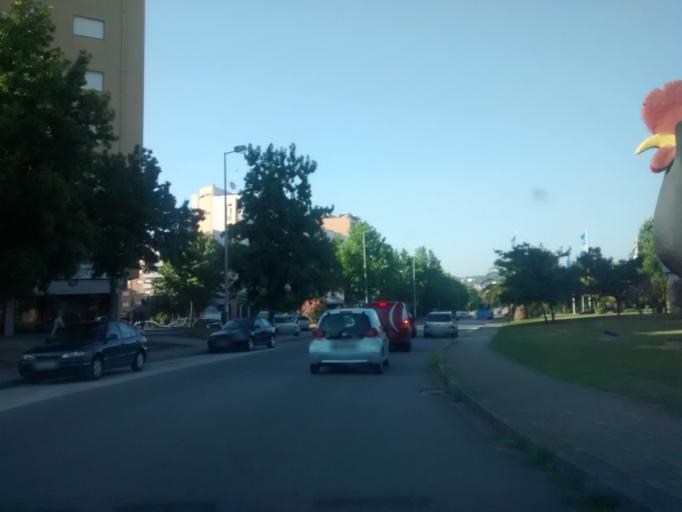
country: PT
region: Braga
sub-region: Braga
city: Braga
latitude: 41.5487
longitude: -8.4031
